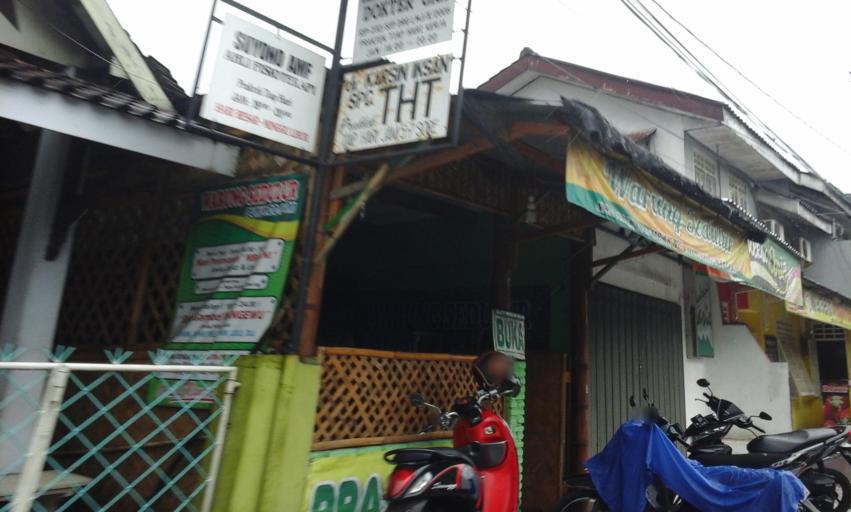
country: ID
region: East Java
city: Lumajang
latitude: -8.1332
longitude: 113.2262
